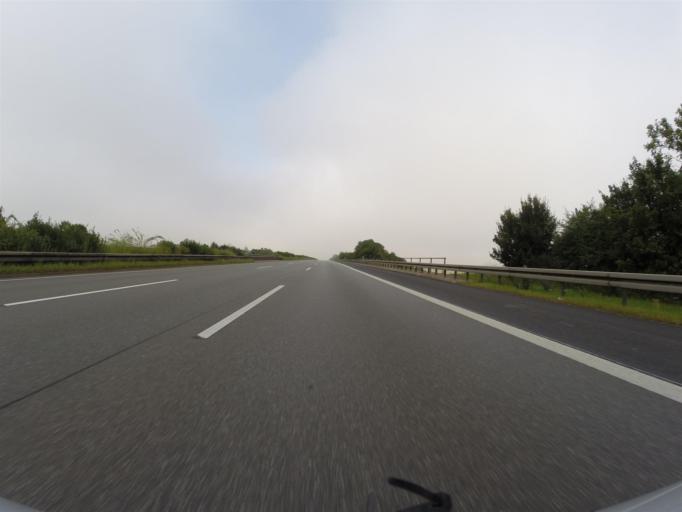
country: DE
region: Thuringia
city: Emleben
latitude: 50.9014
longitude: 10.7113
